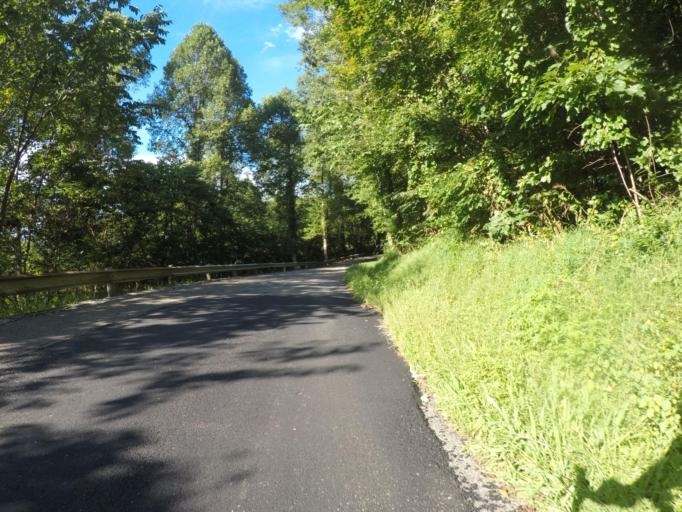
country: US
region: West Virginia
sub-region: Cabell County
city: Huntington
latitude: 38.4532
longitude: -82.4663
